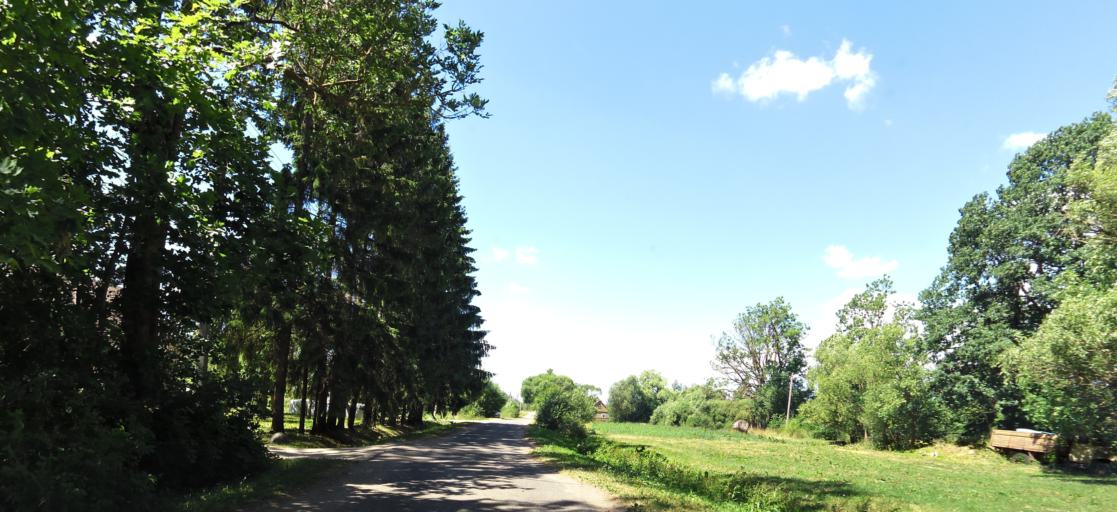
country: LT
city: Kupiskis
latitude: 55.9701
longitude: 24.9997
